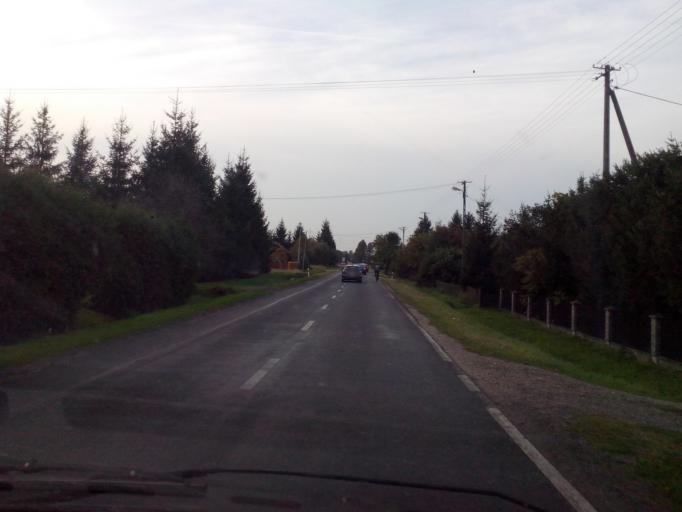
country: PL
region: Subcarpathian Voivodeship
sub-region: Powiat strzyzowski
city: Strzyzow
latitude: 49.8388
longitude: 21.8223
